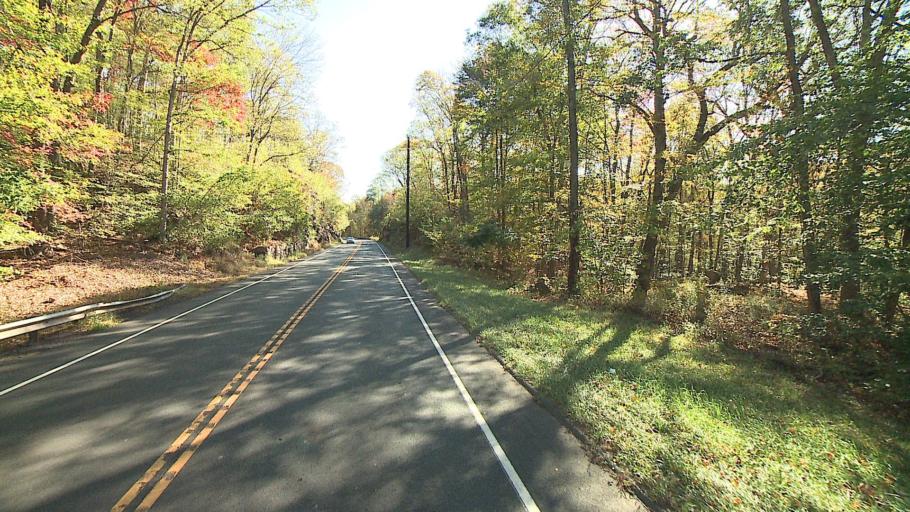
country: US
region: Connecticut
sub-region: Middlesex County
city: Higganum
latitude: 41.5603
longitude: -72.5708
